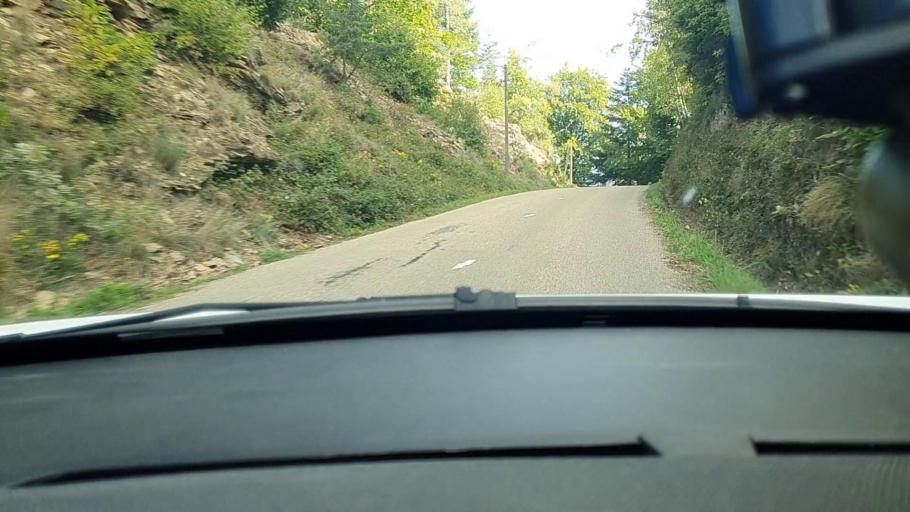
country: FR
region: Rhone-Alpes
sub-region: Departement de l'Ardeche
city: Les Vans
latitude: 44.4261
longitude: 4.0229
